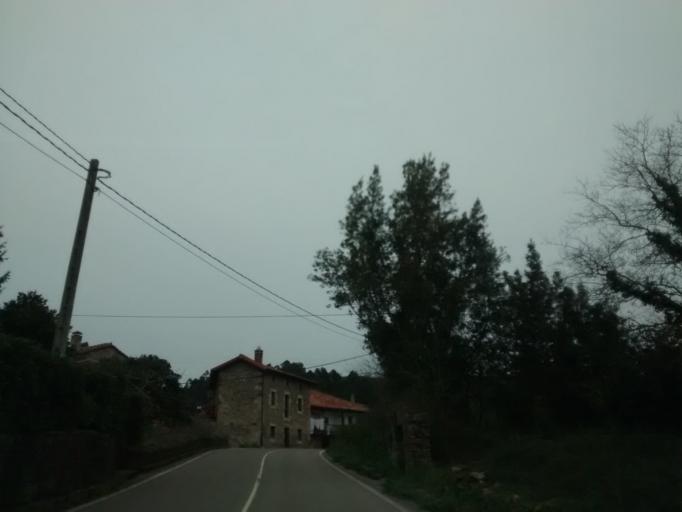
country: ES
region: Cantabria
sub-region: Provincia de Cantabria
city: Lierganes
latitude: 43.3475
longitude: -3.7327
